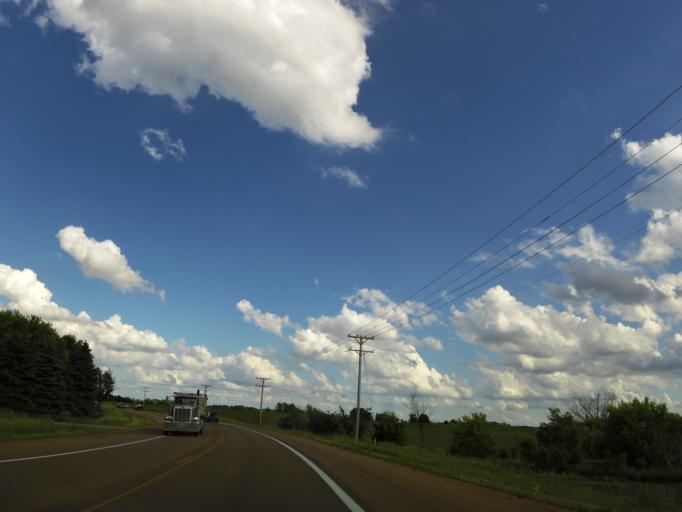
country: US
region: Minnesota
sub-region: Carver County
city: Waconia
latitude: 44.8215
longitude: -93.7400
